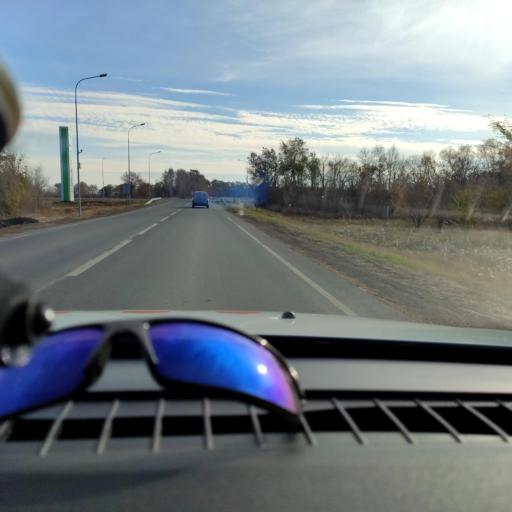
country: RU
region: Samara
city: Samara
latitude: 53.0861
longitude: 50.1394
